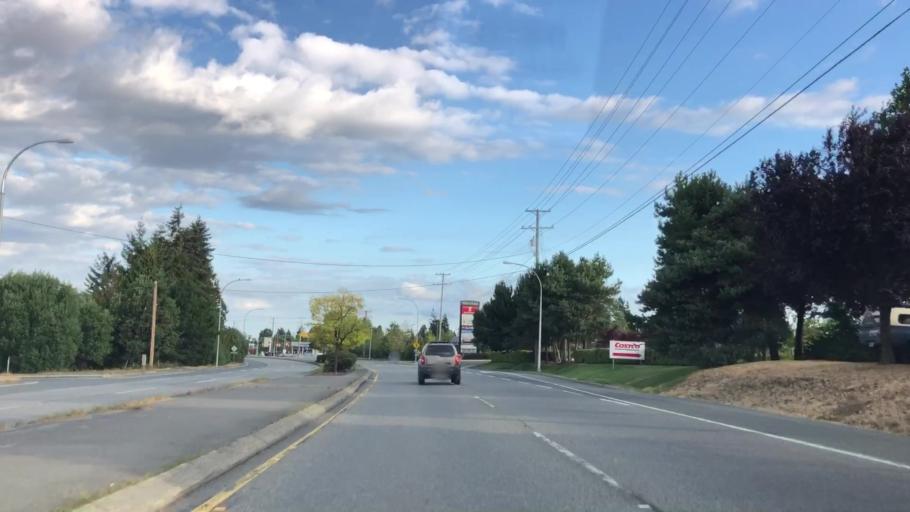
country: CA
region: British Columbia
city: Nanaimo
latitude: 49.2360
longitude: -124.0456
